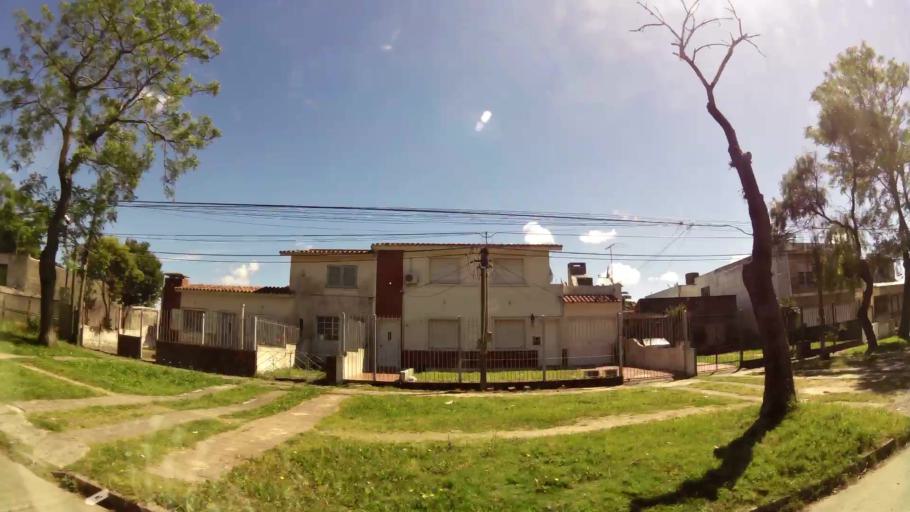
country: UY
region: Canelones
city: Paso de Carrasco
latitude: -34.8429
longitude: -56.1239
